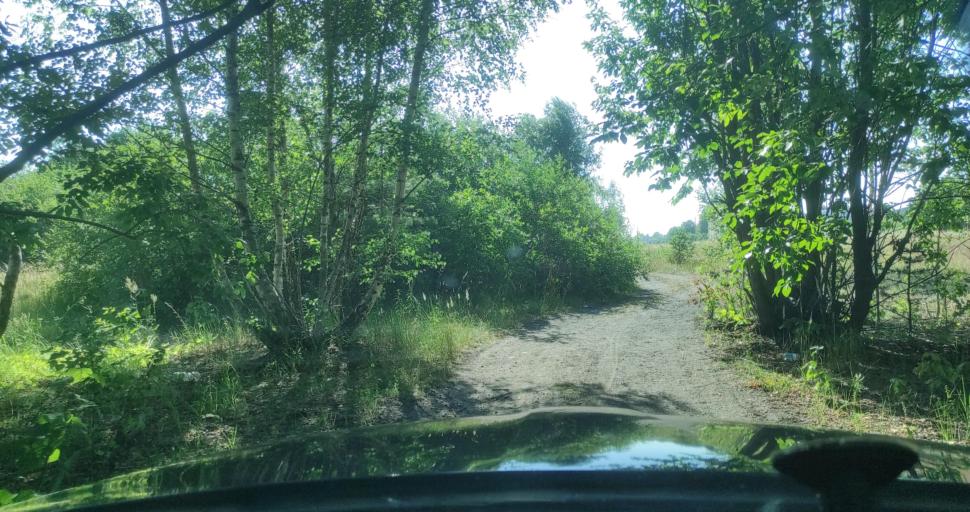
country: LV
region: Skrunda
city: Skrunda
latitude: 56.6802
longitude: 22.0213
